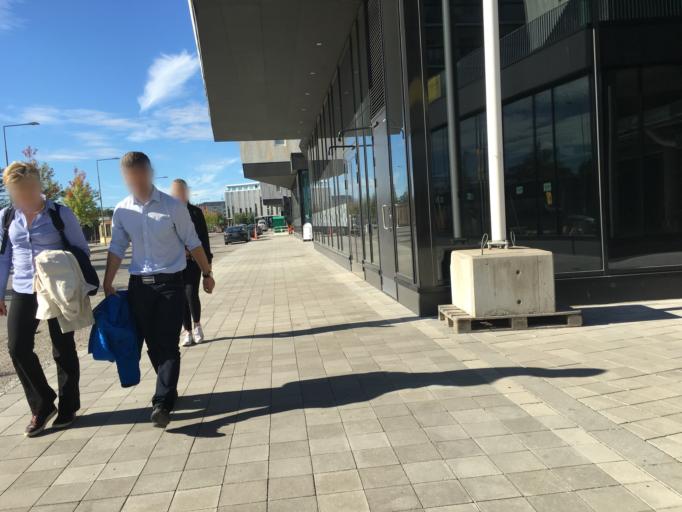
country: SE
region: Uppsala
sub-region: Uppsala Kommun
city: Uppsala
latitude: 59.8574
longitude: 17.6509
